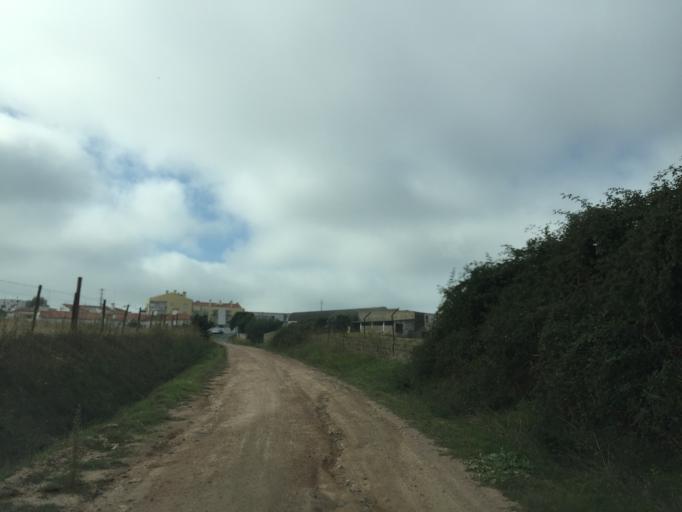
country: PT
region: Portalegre
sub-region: Fronteira
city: Fronteira
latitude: 39.0552
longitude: -7.6412
